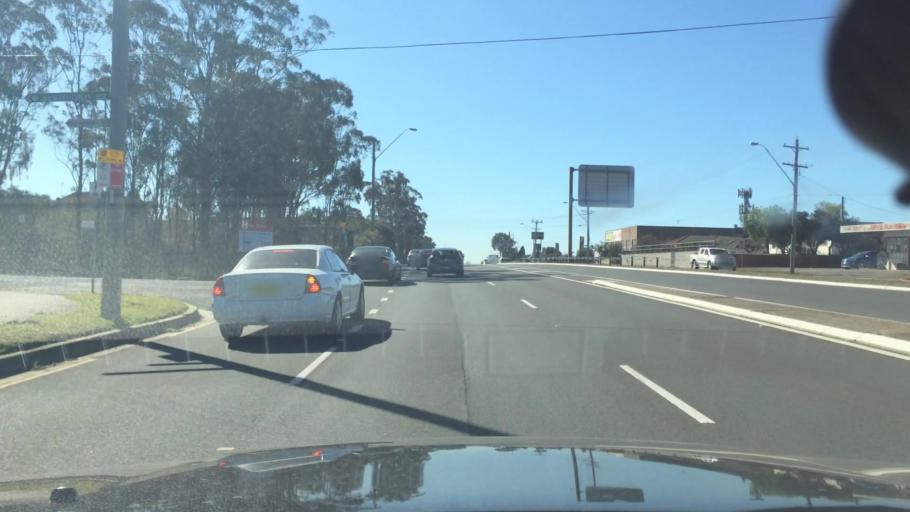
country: AU
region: New South Wales
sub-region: Campbelltown Municipality
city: Glenfield
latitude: -33.9575
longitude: 150.8877
